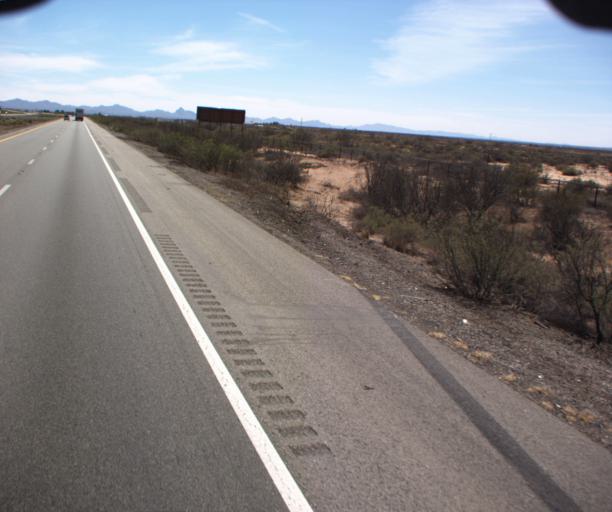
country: US
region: New Mexico
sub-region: Hidalgo County
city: Lordsburg
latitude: 32.2677
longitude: -109.2410
